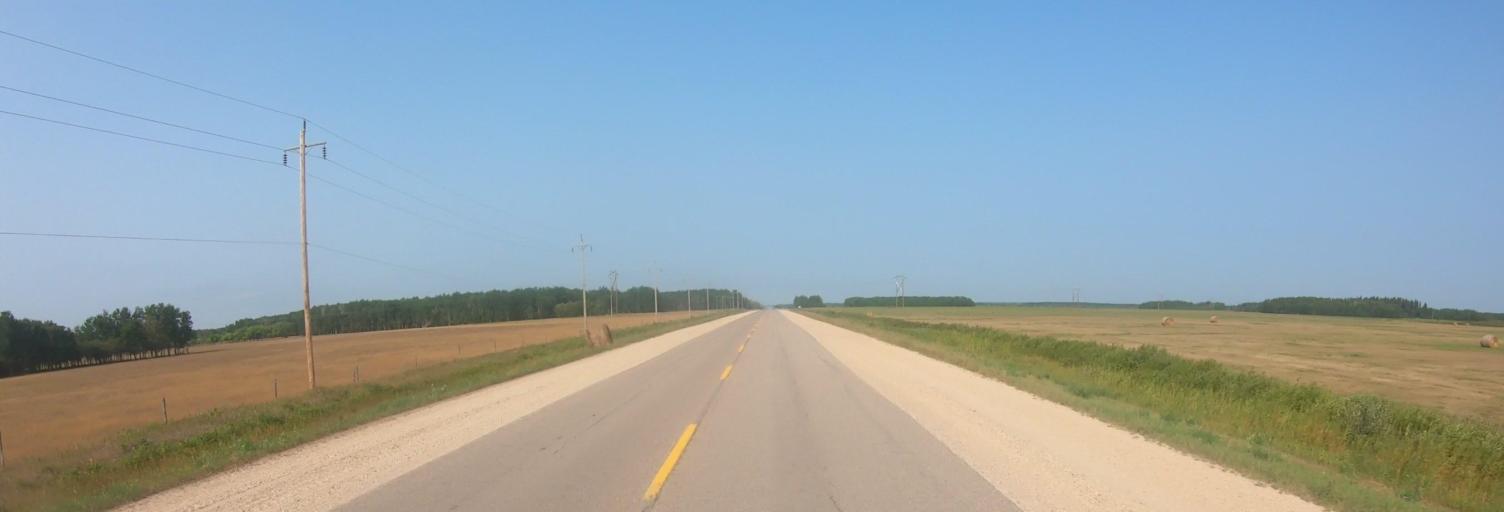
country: US
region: Minnesota
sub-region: Roseau County
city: Roseau
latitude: 49.0236
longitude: -95.5765
